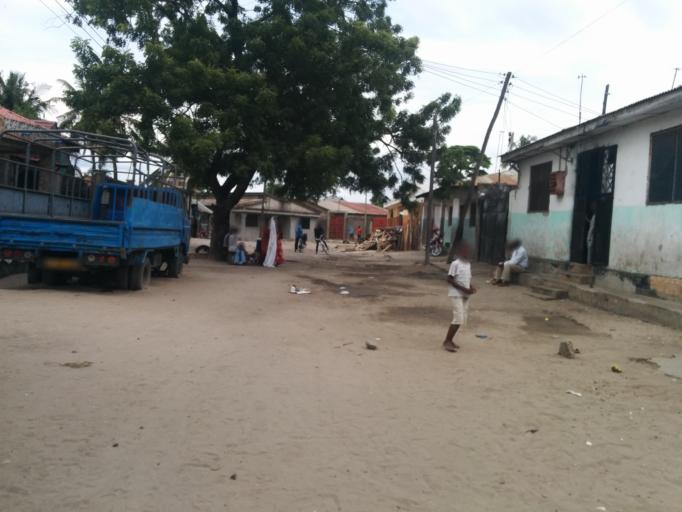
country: TZ
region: Dar es Salaam
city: Dar es Salaam
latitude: -6.8671
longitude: 39.2506
